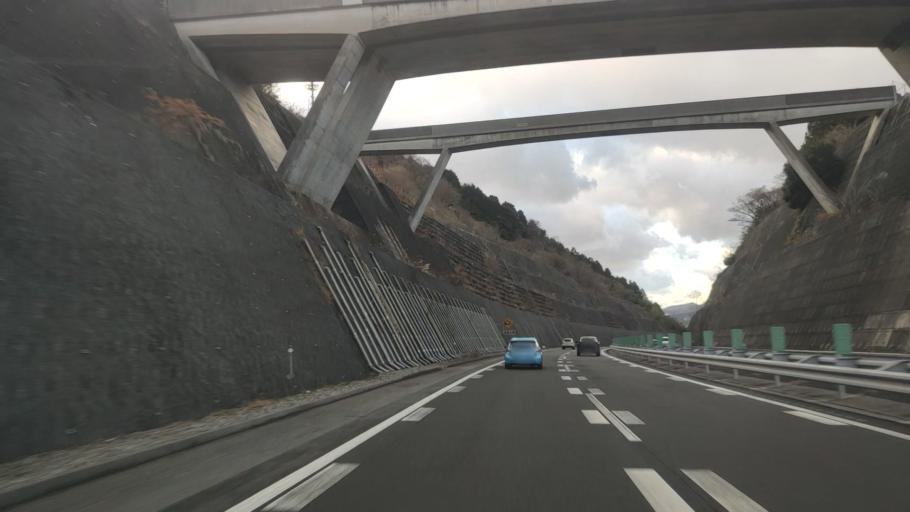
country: JP
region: Ehime
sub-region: Shikoku-chuo Shi
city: Matsuyama
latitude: 33.7906
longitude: 132.9166
